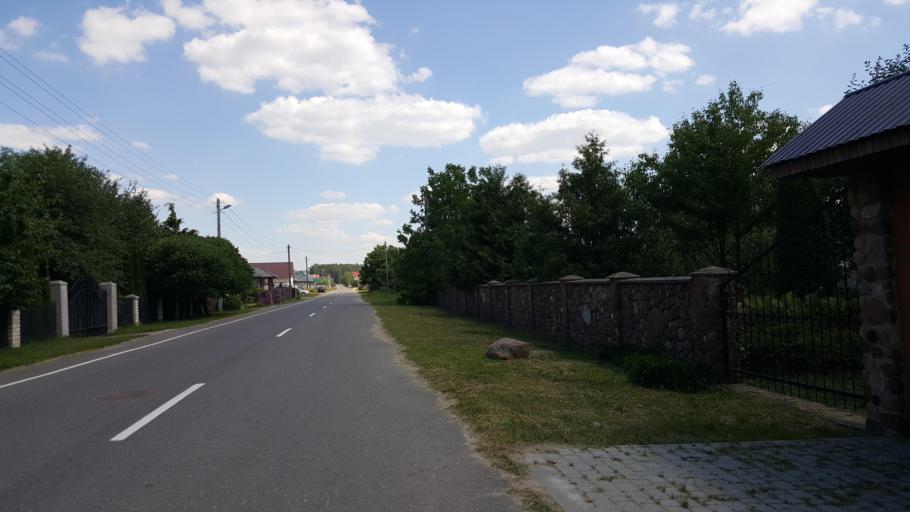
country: BY
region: Brest
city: Kamyanyets
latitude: 52.3942
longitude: 23.8077
